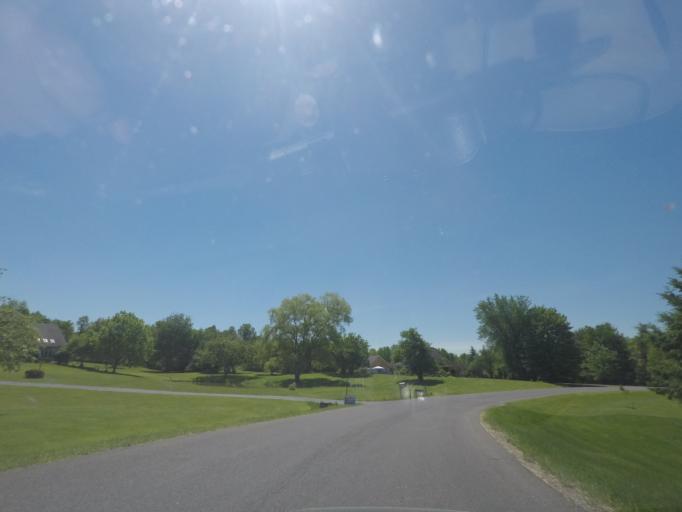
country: US
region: New York
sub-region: Saratoga County
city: Country Knolls
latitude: 42.9395
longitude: -73.7597
